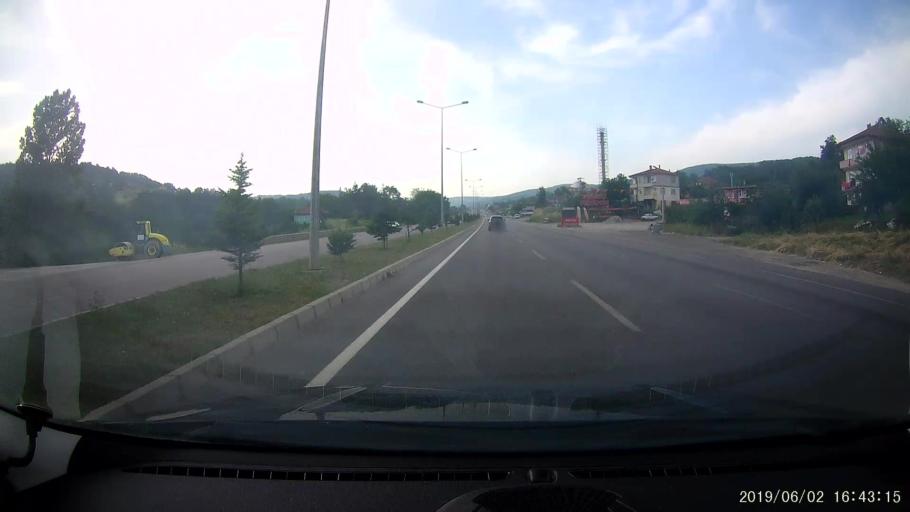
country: TR
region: Samsun
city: Kavak
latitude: 41.1322
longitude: 36.1309
